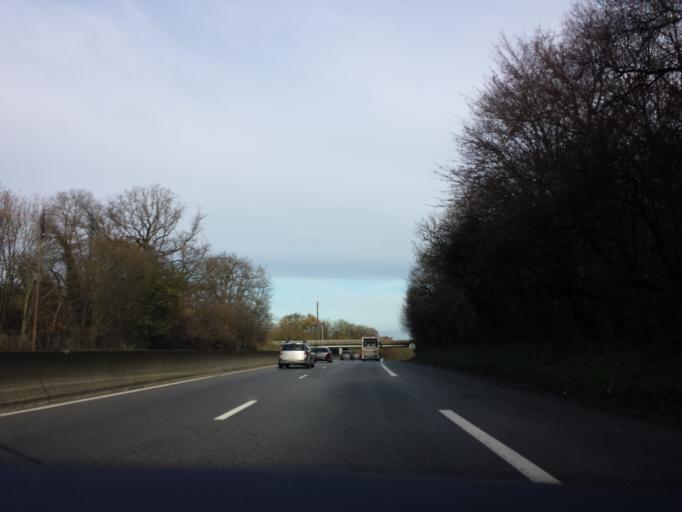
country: FR
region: Ile-de-France
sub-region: Departement des Yvelines
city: Orgeval
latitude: 48.8997
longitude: 2.0053
